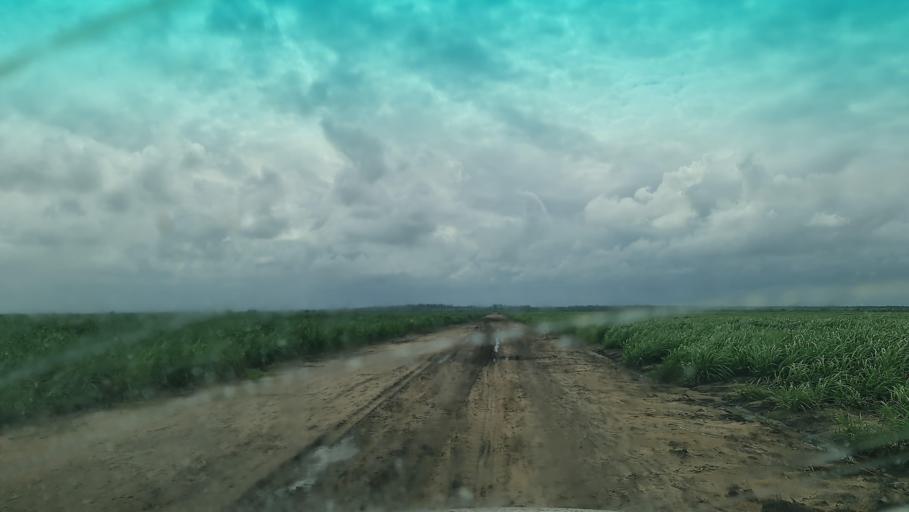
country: MZ
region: Maputo
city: Manhica
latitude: -25.4528
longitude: 32.8261
